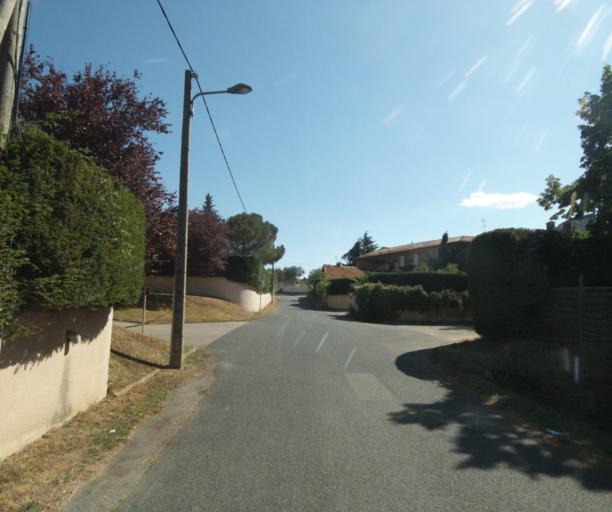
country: FR
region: Rhone-Alpes
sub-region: Departement du Rhone
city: La Tour-de-Salvagny
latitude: 45.8343
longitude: 4.7061
